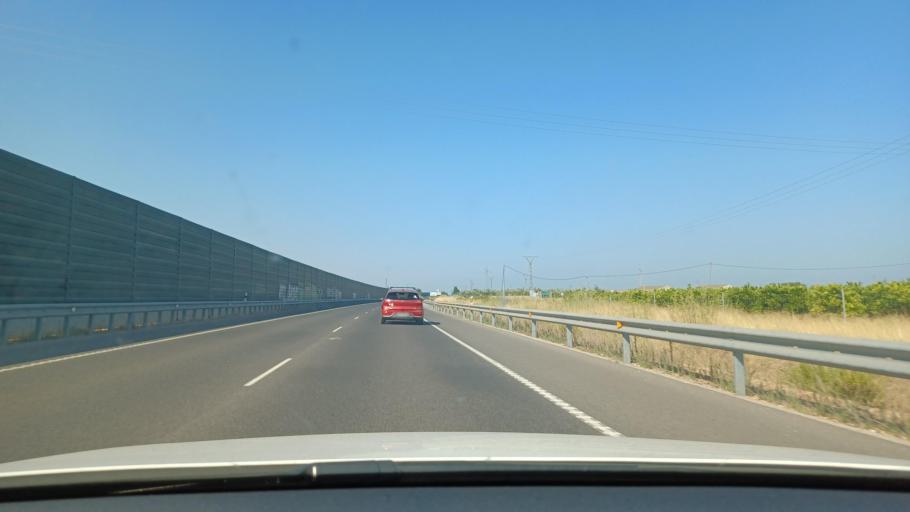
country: ES
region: Valencia
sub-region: Provincia de Castello
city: Benicarlo
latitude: 40.4231
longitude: 0.3922
